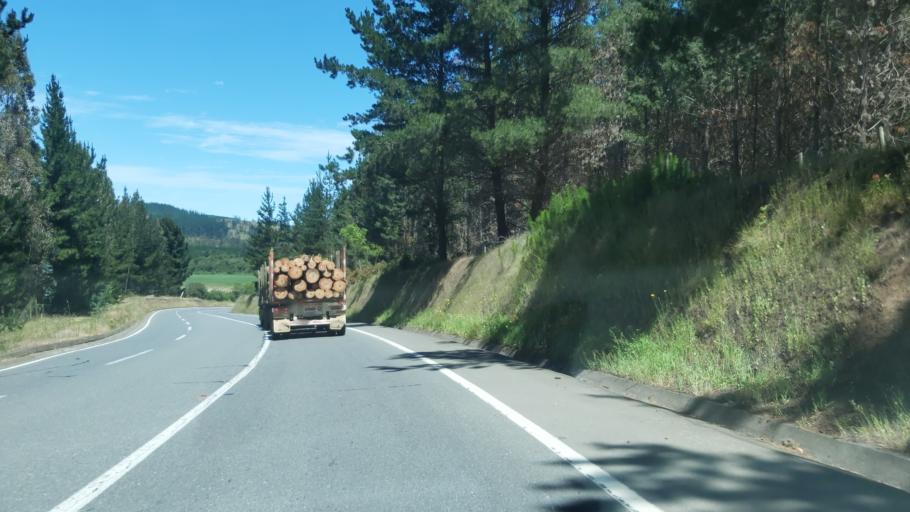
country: CL
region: Maule
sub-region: Provincia de Talca
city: Constitucion
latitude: -35.1528
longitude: -72.2209
